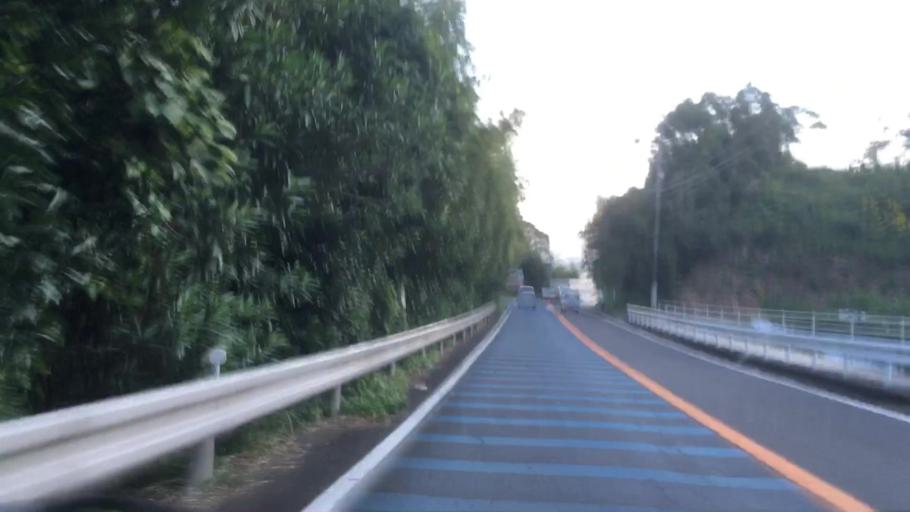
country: JP
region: Nagasaki
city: Sasebo
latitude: 33.0363
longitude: 129.7450
